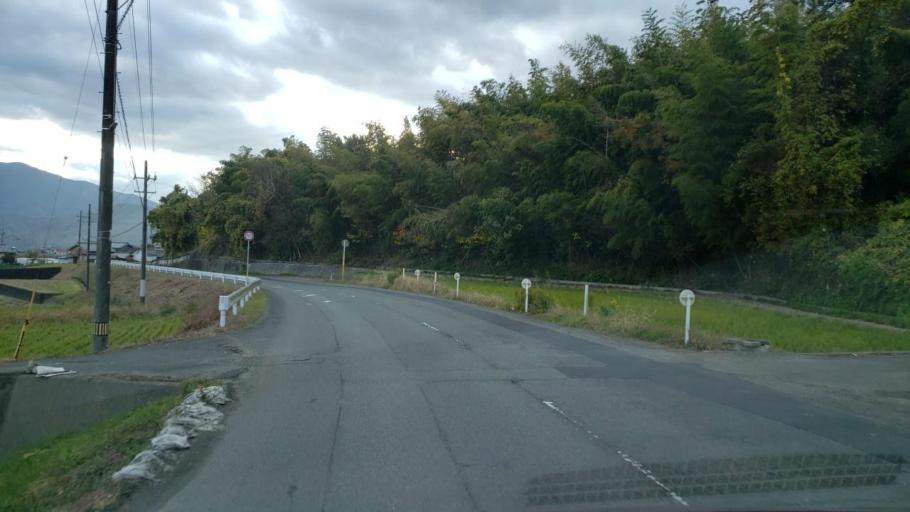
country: JP
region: Tokushima
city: Wakimachi
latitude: 34.0975
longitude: 134.2181
